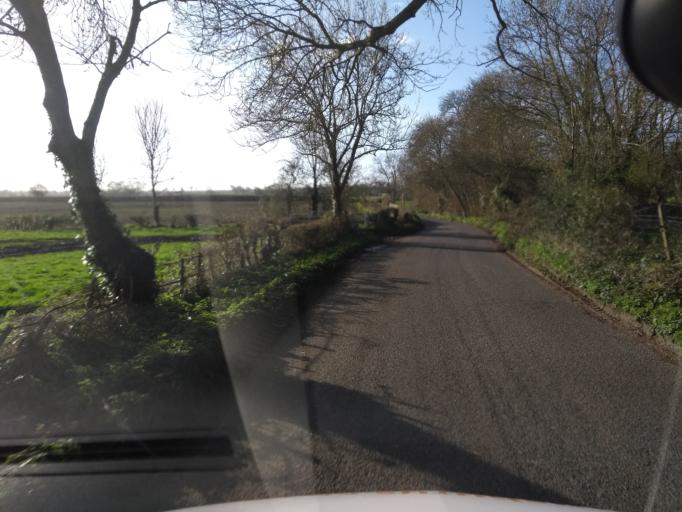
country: GB
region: England
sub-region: Somerset
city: Wedmore
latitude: 51.1464
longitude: -2.8327
